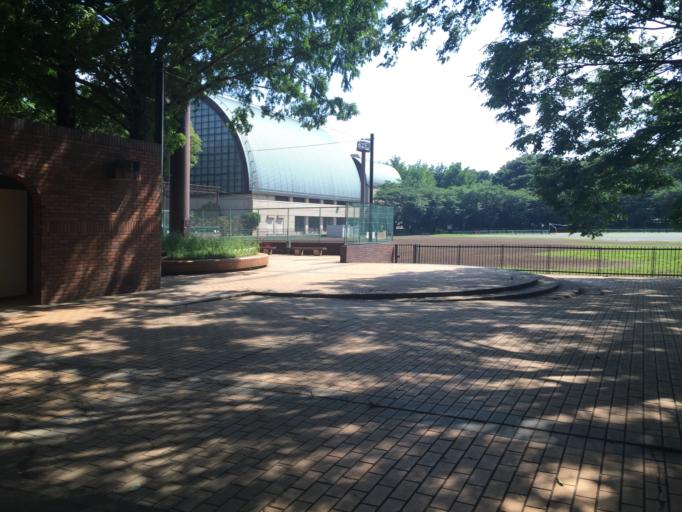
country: JP
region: Tokyo
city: Kokubunji
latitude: 35.7239
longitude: 139.4630
